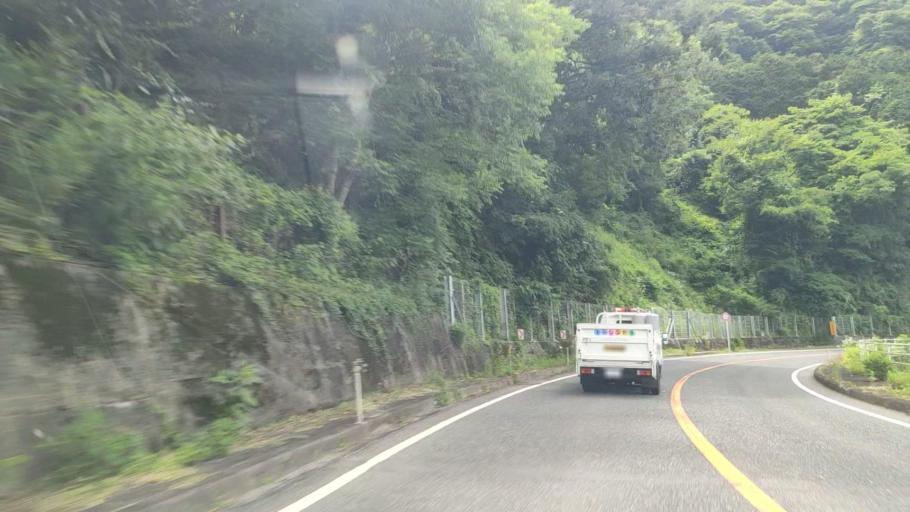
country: JP
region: Okayama
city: Niimi
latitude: 35.0810
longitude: 133.6523
